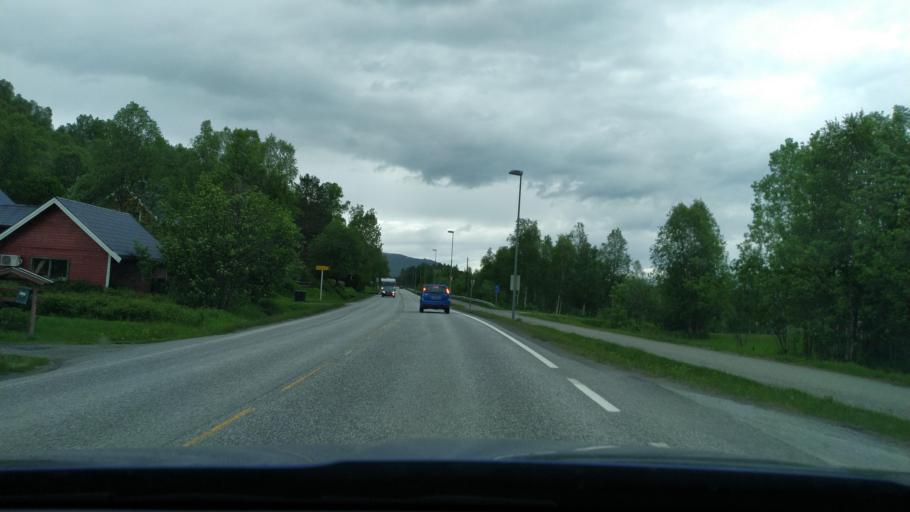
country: NO
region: Troms
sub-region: Malselv
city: Moen
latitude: 69.0341
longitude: 18.5060
